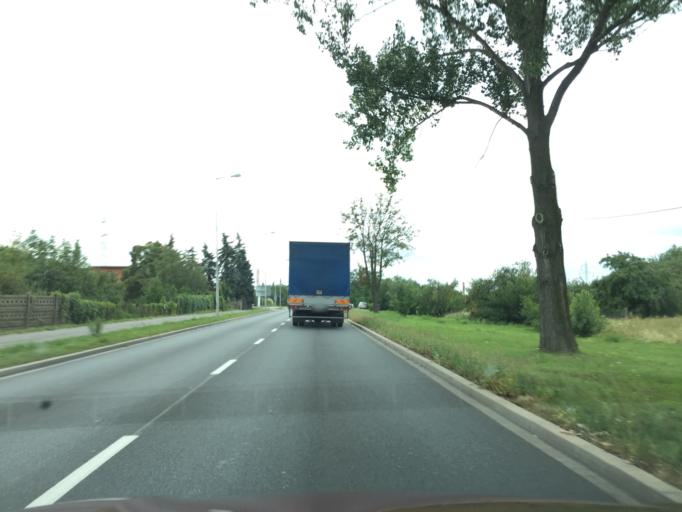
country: PL
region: Greater Poland Voivodeship
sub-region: Kalisz
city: Kalisz
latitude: 51.7904
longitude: 18.0907
